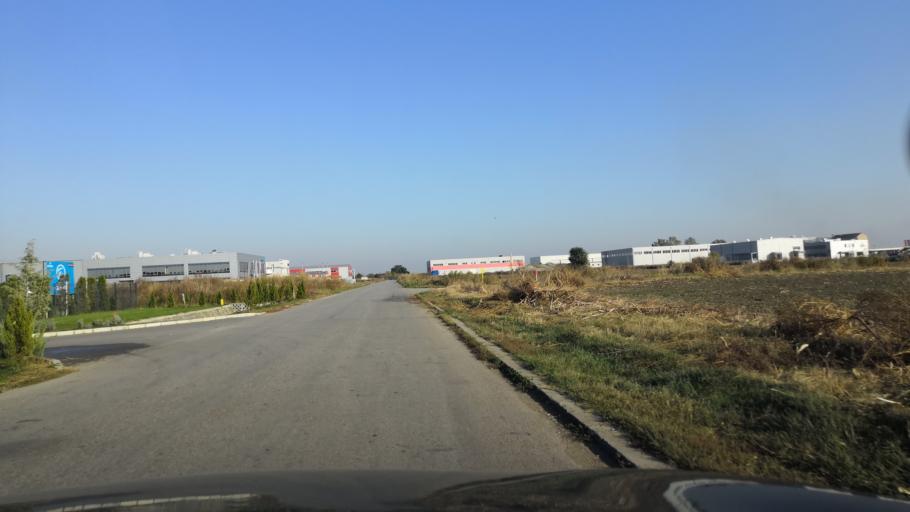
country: RS
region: Autonomna Pokrajina Vojvodina
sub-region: Sremski Okrug
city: Stara Pazova
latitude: 44.9900
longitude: 20.1973
